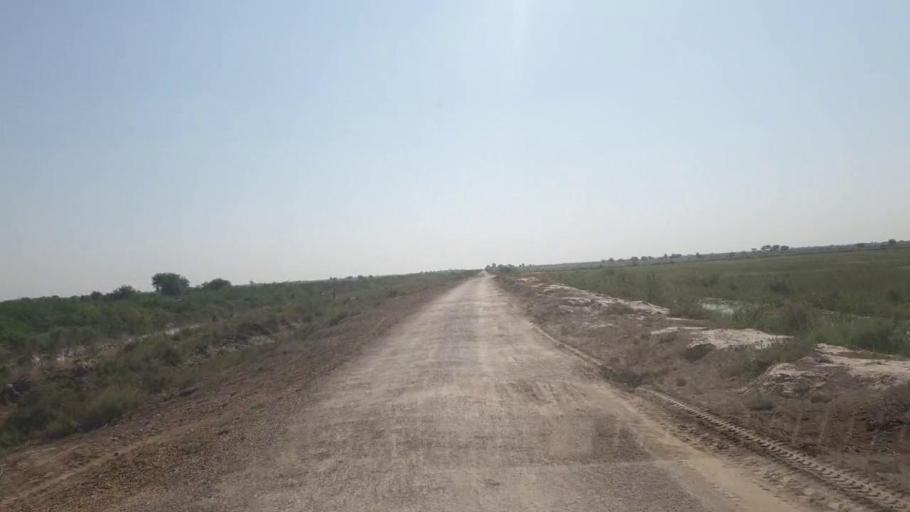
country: PK
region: Sindh
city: Tando Bago
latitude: 24.8626
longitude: 69.1643
